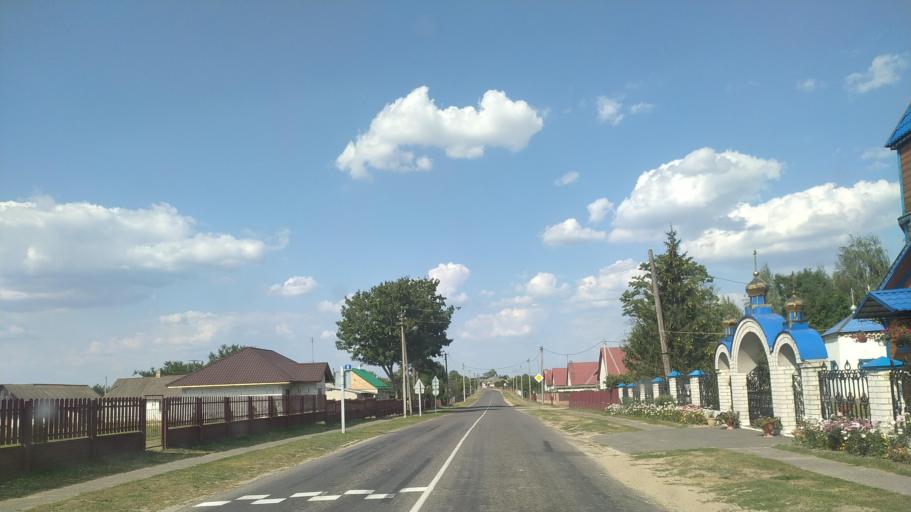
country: BY
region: Brest
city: Drahichyn
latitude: 52.1167
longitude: 25.1163
